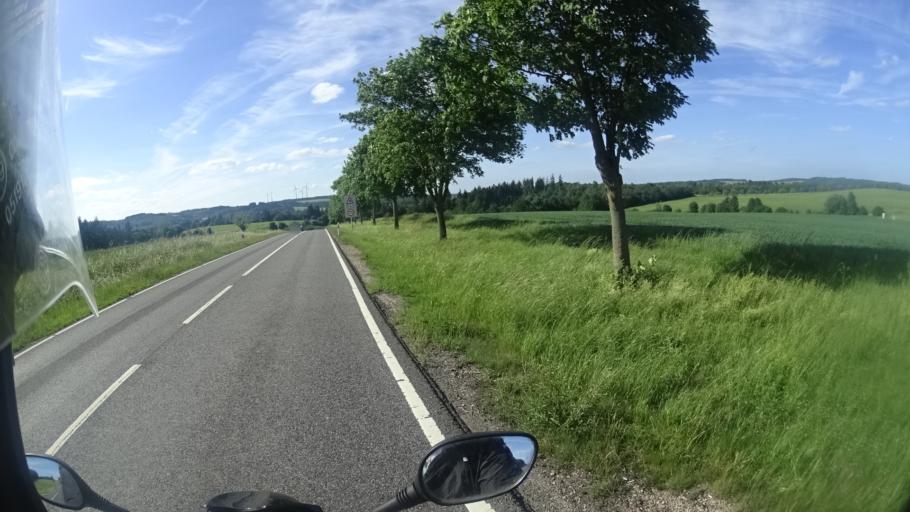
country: DE
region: Hesse
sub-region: Regierungsbezirk Darmstadt
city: Bad Schwalbach
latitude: 50.1299
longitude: 8.0773
